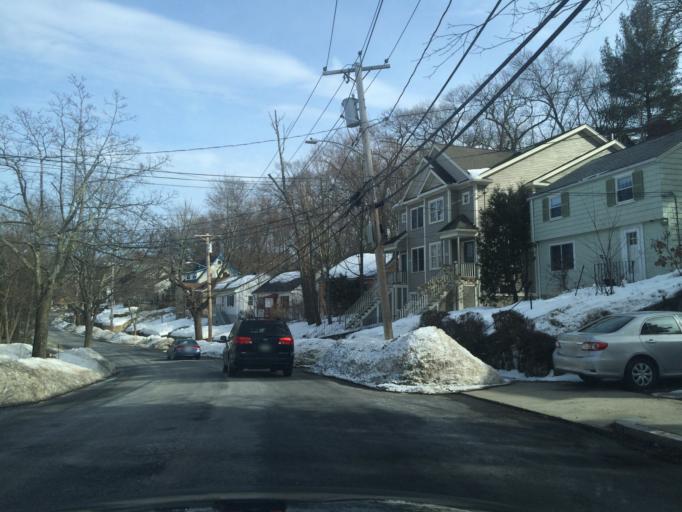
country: US
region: Massachusetts
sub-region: Middlesex County
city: Belmont
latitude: 42.4239
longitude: -71.1866
